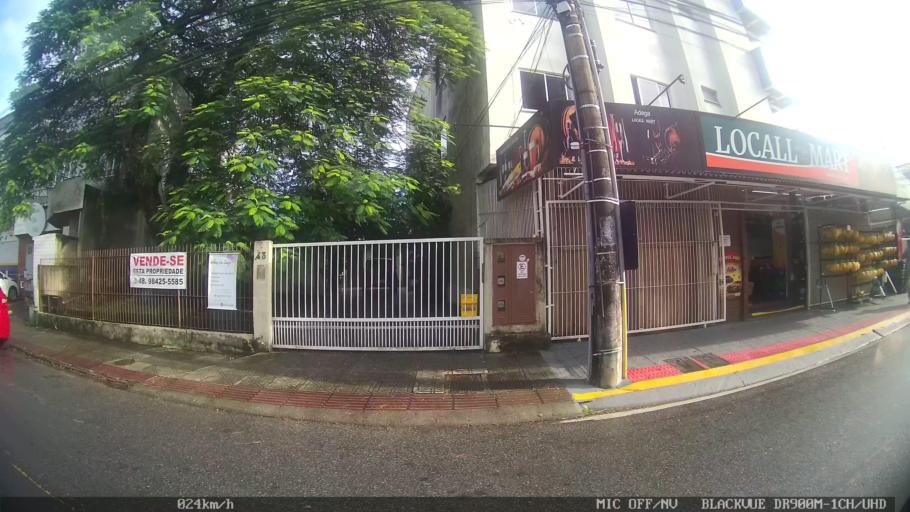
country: BR
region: Santa Catarina
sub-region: Sao Jose
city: Campinas
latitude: -27.6037
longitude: -48.6271
